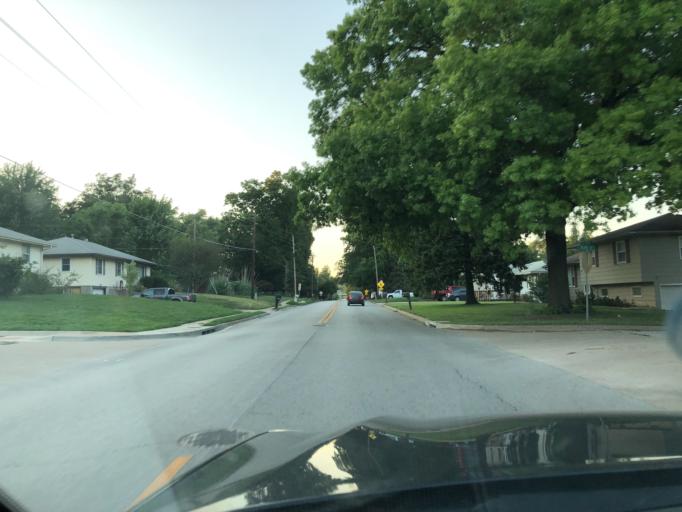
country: US
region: Kansas
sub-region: Leavenworth County
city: Leavenworth
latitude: 39.3193
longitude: -94.9506
